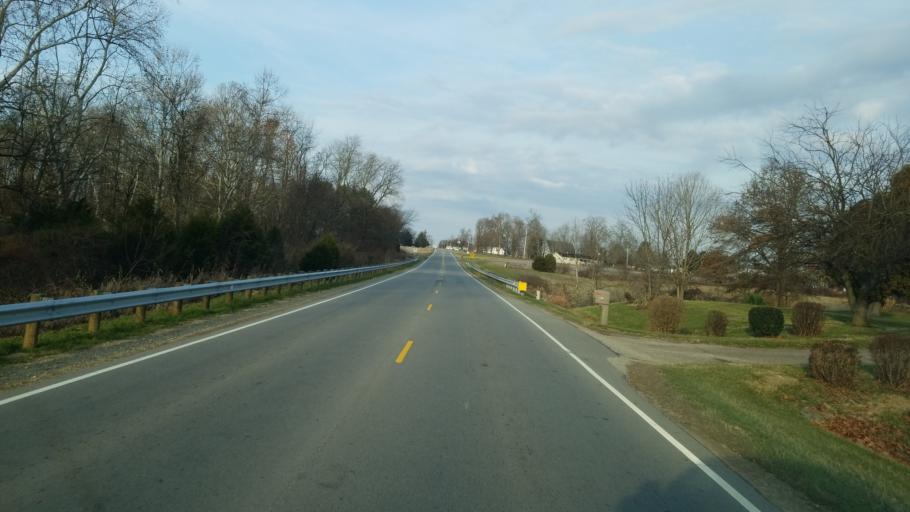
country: US
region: Ohio
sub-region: Ross County
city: Chillicothe
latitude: 39.2889
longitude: -82.8713
